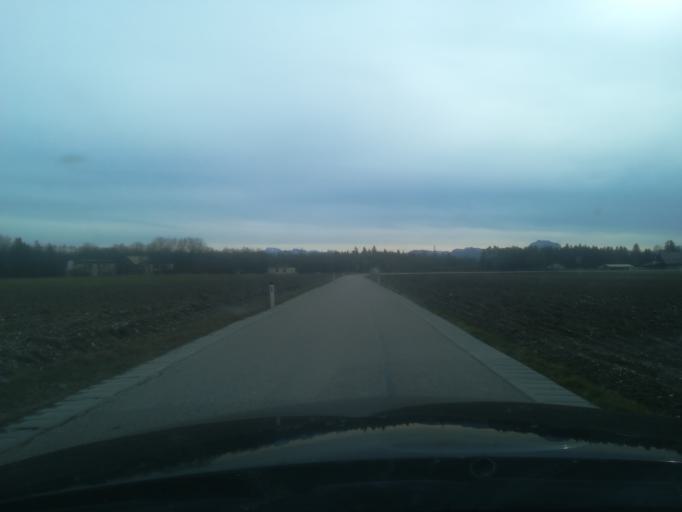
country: AT
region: Upper Austria
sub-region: Wels-Land
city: Bad Wimsbach-Neydharting
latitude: 48.0974
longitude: 13.9210
